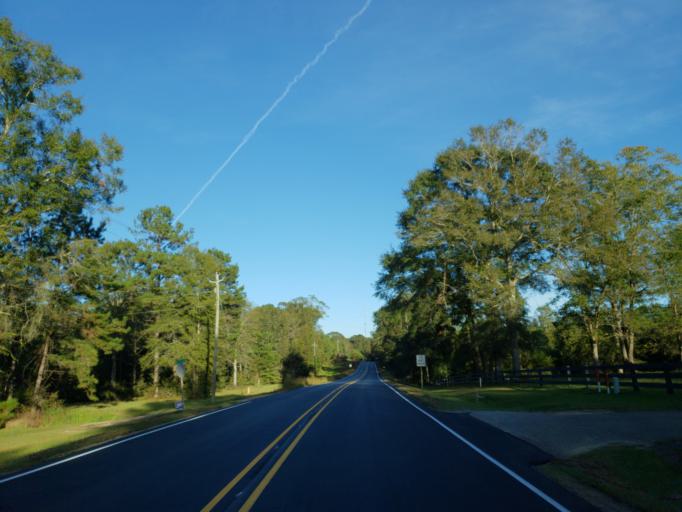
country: US
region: Mississippi
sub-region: Perry County
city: Richton
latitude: 31.3469
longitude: -88.7714
